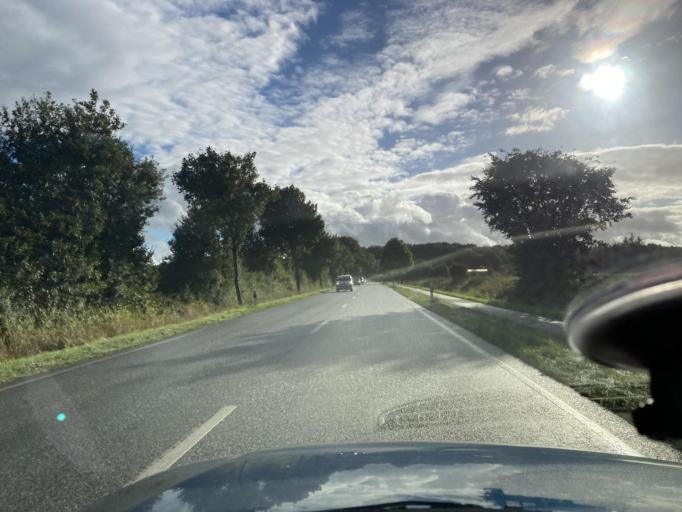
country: DE
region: Schleswig-Holstein
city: Fockbek
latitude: 54.2832
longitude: 9.5766
